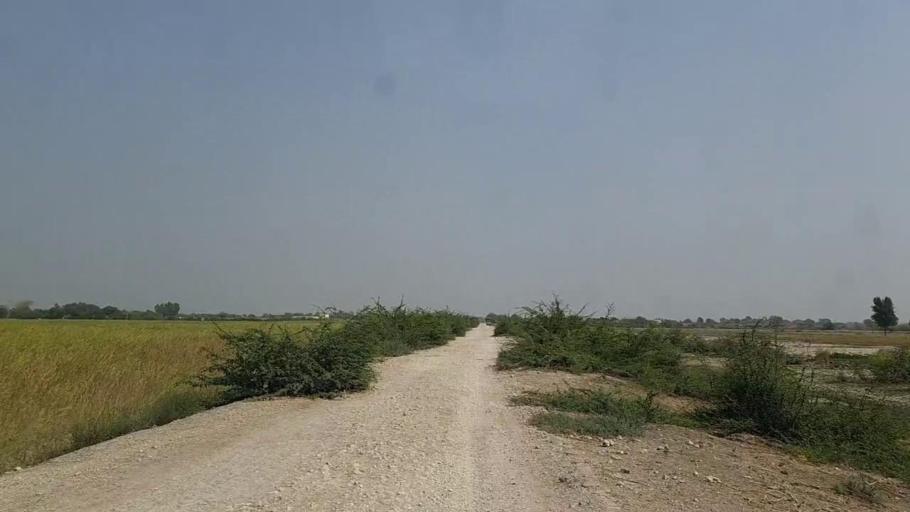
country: PK
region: Sindh
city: Naukot
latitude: 24.8125
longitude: 69.3789
